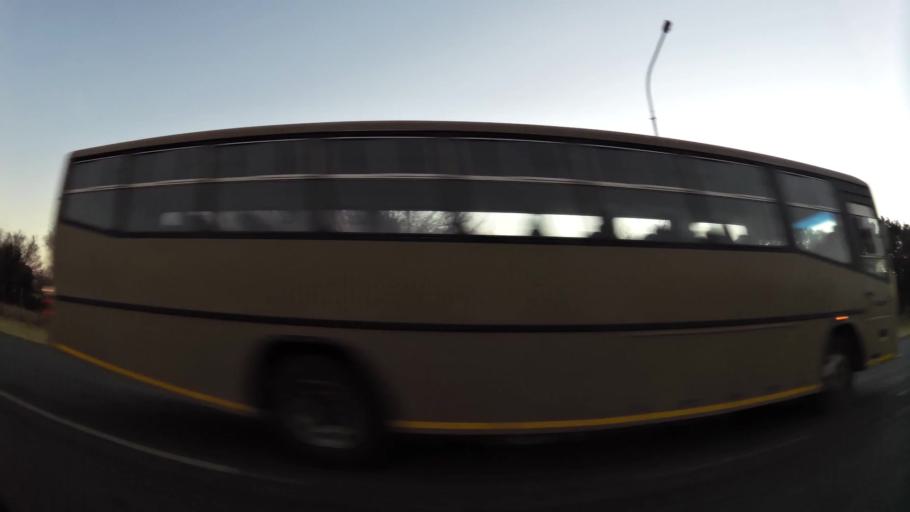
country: ZA
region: North-West
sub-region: Dr Kenneth Kaunda District Municipality
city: Potchefstroom
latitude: -26.6914
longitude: 27.0779
